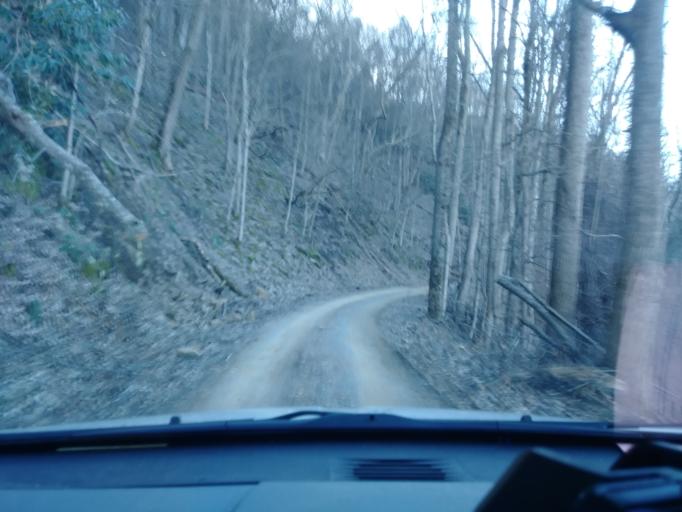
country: US
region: Tennessee
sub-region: Greene County
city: Tusculum
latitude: 36.0797
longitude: -82.6854
